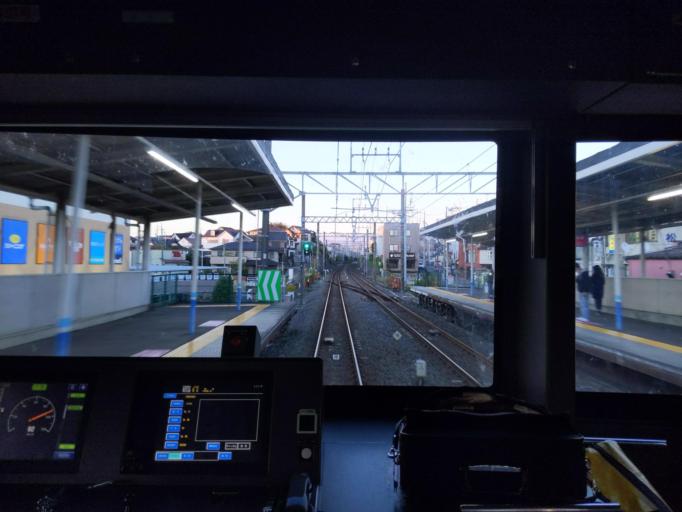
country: JP
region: Chiba
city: Funabashi
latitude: 35.7420
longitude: 139.9923
